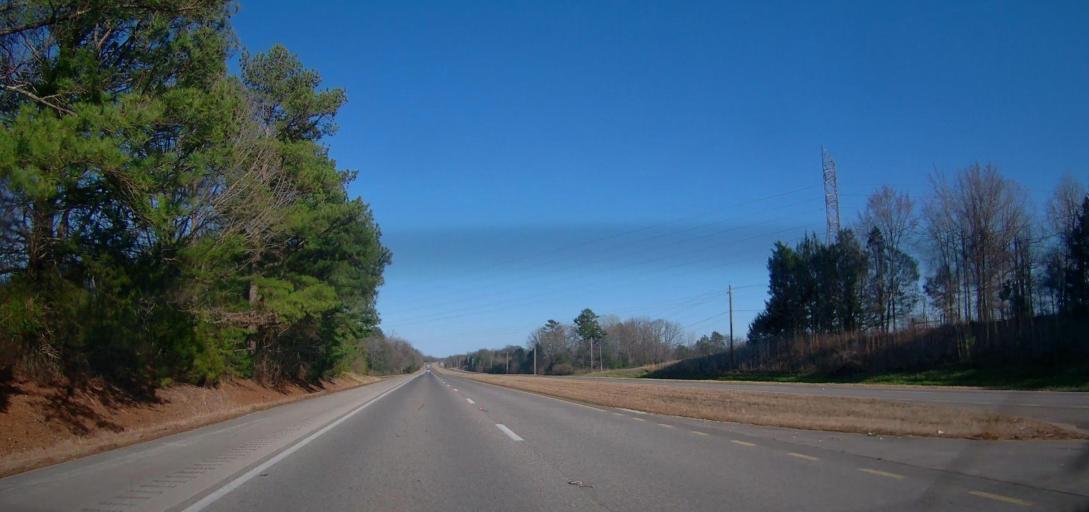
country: US
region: Alabama
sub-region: Colbert County
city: Cherokee
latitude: 34.7337
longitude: -87.8850
